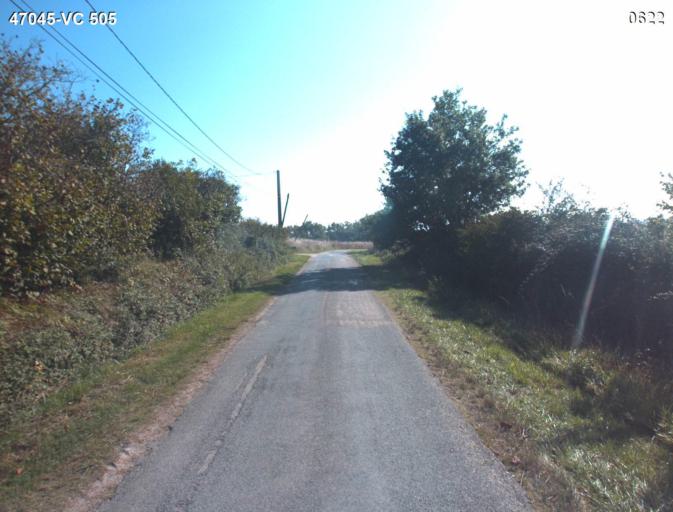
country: FR
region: Aquitaine
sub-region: Departement du Lot-et-Garonne
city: Nerac
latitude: 44.1528
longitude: 0.4039
